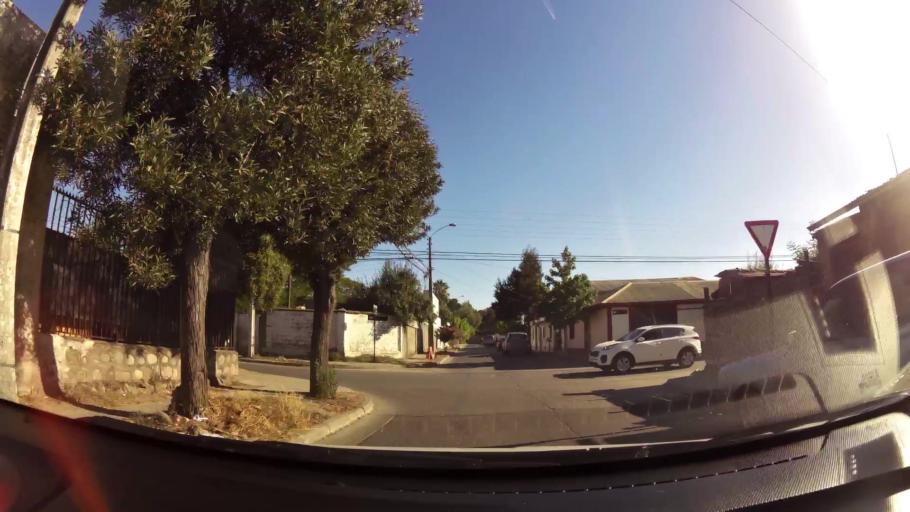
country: CL
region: O'Higgins
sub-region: Provincia de Colchagua
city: Chimbarongo
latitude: -34.5927
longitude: -70.9931
